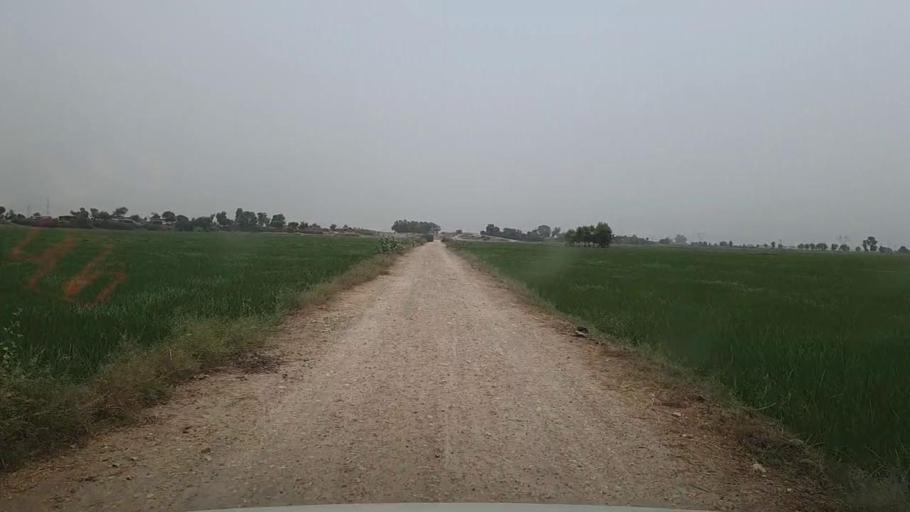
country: PK
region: Sindh
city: Sita Road
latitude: 27.0557
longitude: 67.8515
